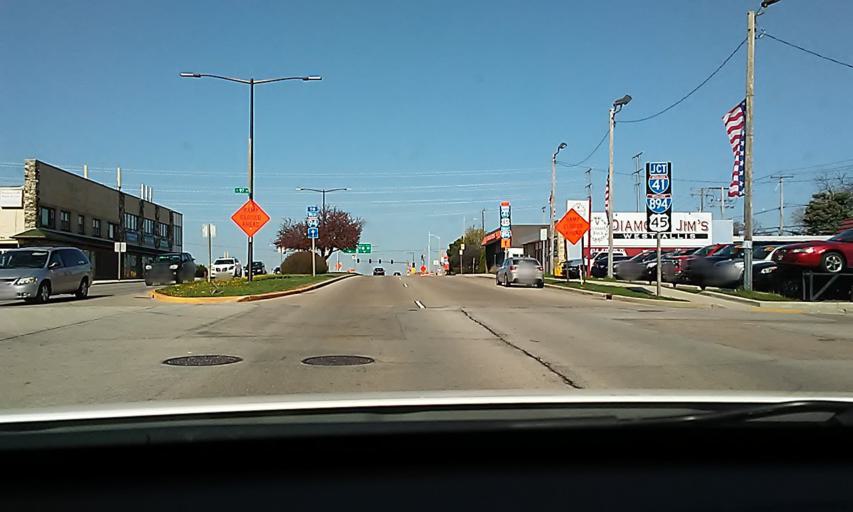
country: US
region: Wisconsin
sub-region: Milwaukee County
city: West Allis
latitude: 43.0166
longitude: -88.0332
